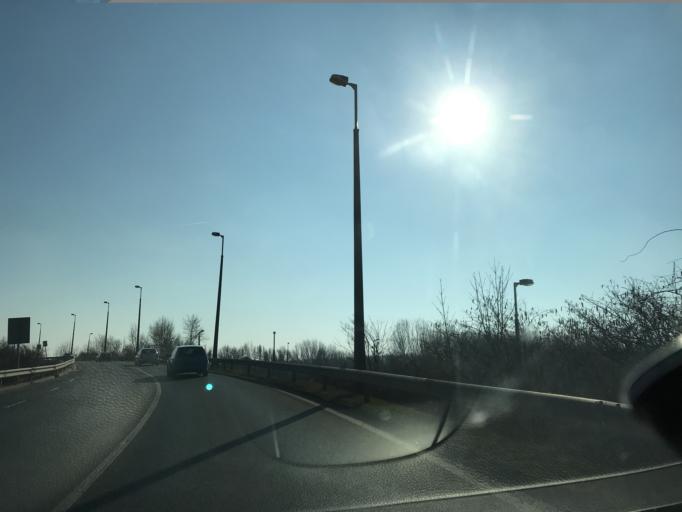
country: HU
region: Gyor-Moson-Sopron
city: Gyor
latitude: 47.6810
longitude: 17.6245
